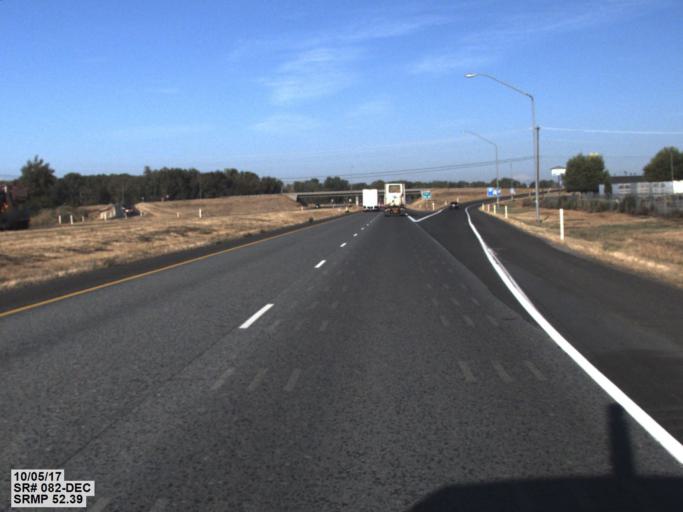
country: US
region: Washington
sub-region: Yakima County
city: Zillah
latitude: 46.4024
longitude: -120.2724
